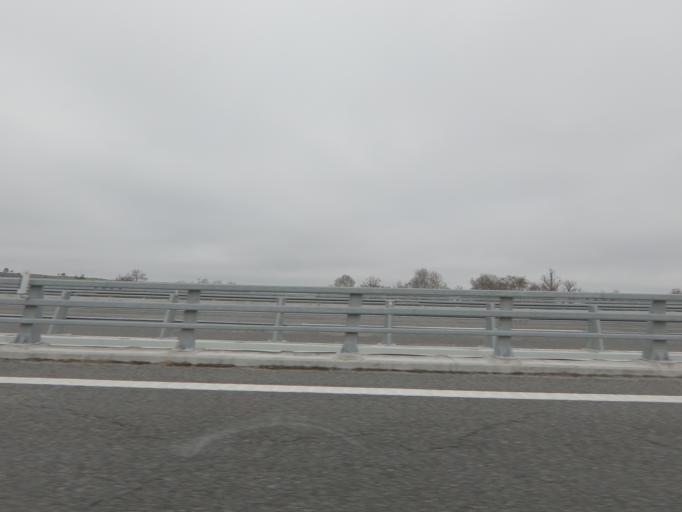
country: PT
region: Vila Real
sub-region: Chaves
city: Chaves
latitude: 41.7967
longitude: -7.4313
